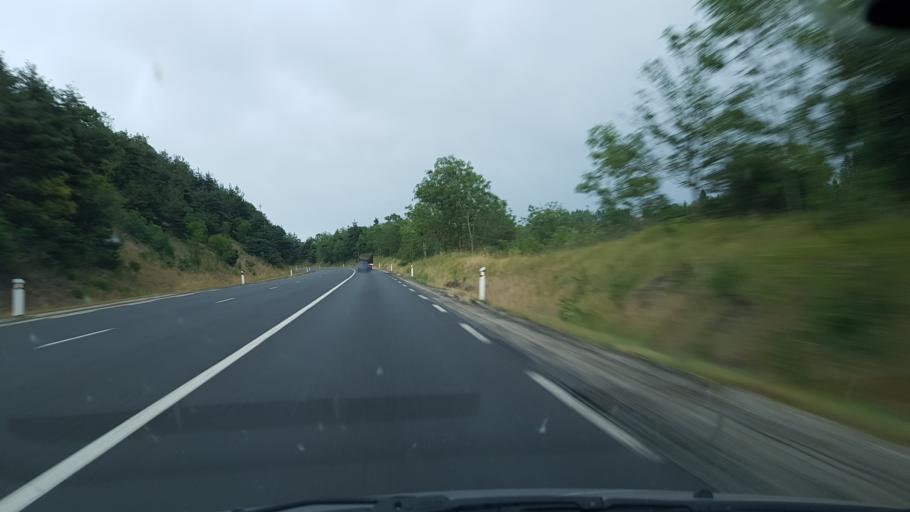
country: FR
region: Auvergne
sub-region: Departement de la Haute-Loire
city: Allegre
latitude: 45.1370
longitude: 3.6157
